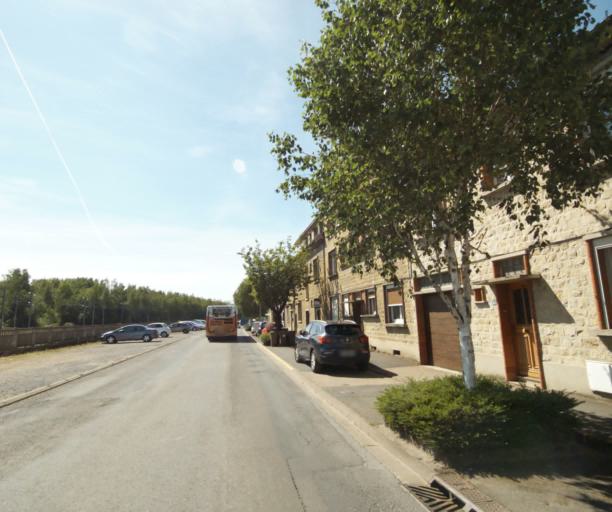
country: FR
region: Champagne-Ardenne
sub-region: Departement des Ardennes
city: Villers-Semeuse
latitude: 49.7501
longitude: 4.7358
